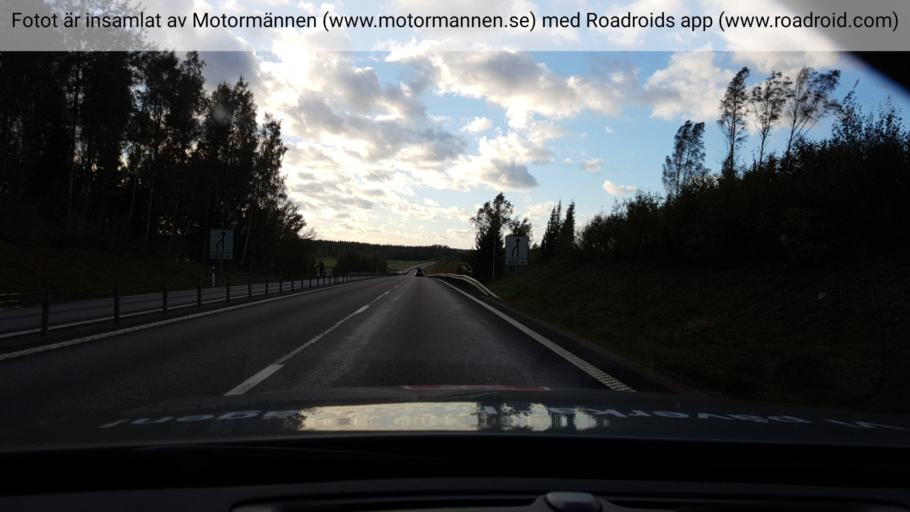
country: SE
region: Vaermland
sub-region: Karlstads Kommun
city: Skattkarr
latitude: 59.3998
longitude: 13.7963
